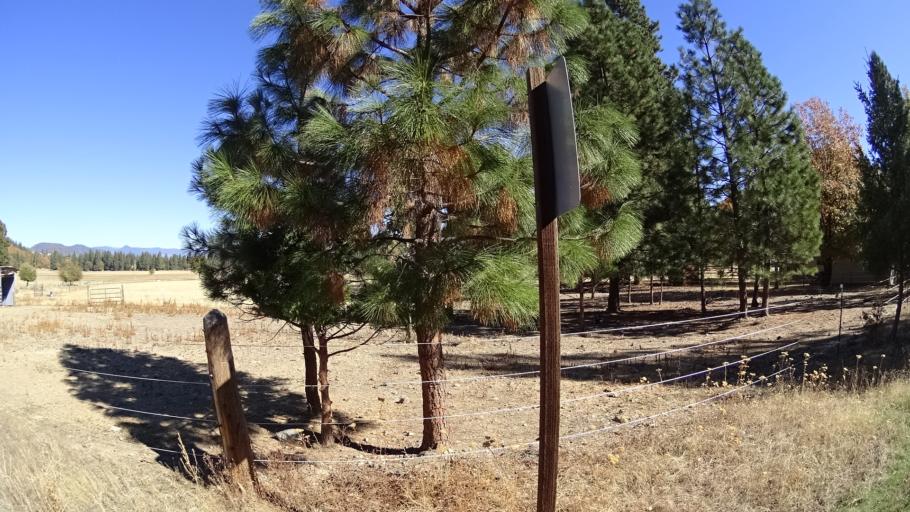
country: US
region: California
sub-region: Siskiyou County
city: Yreka
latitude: 41.5219
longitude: -122.9253
